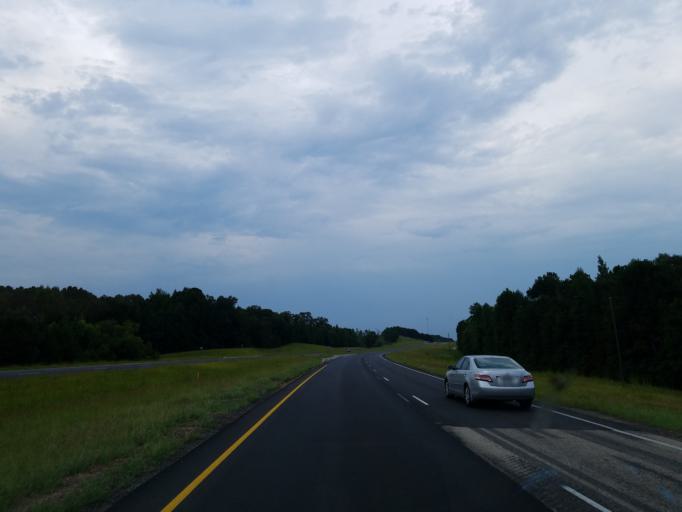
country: US
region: Mississippi
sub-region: Clarke County
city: Quitman
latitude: 32.1138
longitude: -88.7159
